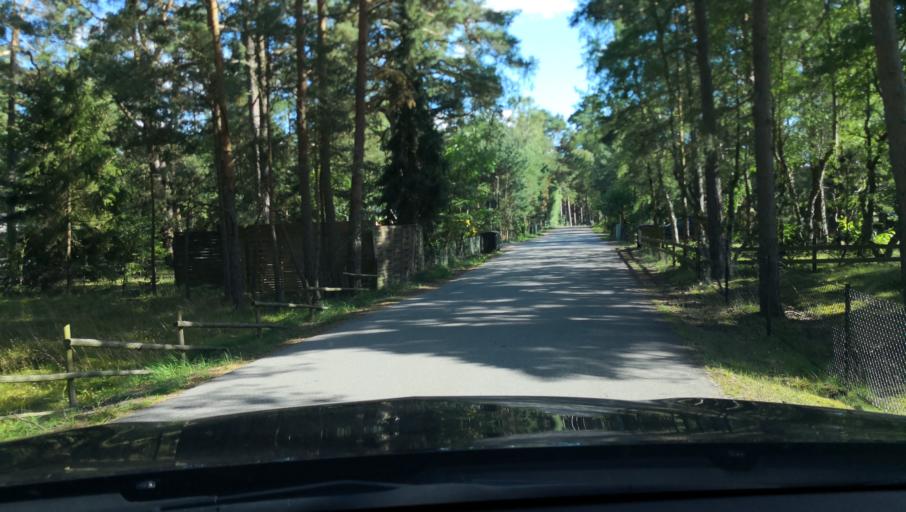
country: SE
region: Skane
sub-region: Simrishamns Kommun
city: Kivik
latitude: 55.7768
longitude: 14.1971
